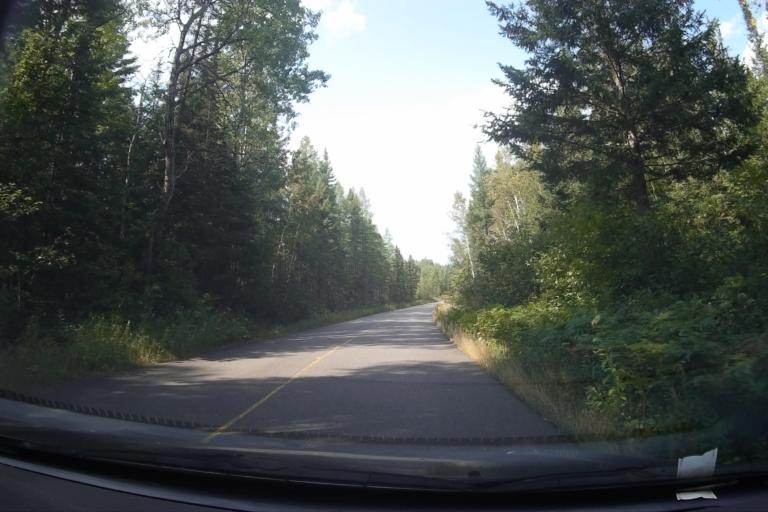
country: CA
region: Ontario
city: Bancroft
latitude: 45.6259
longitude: -78.3508
